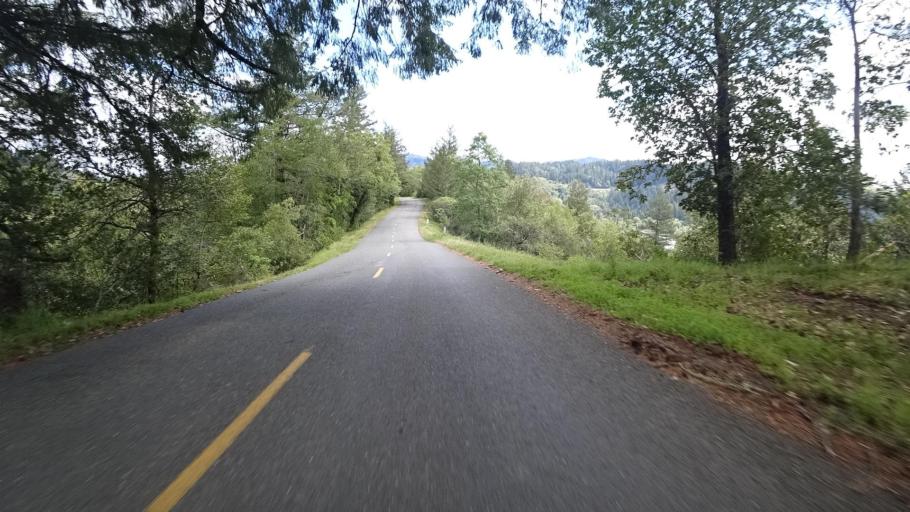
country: US
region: California
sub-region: Humboldt County
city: Redway
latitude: 40.0905
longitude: -123.8072
